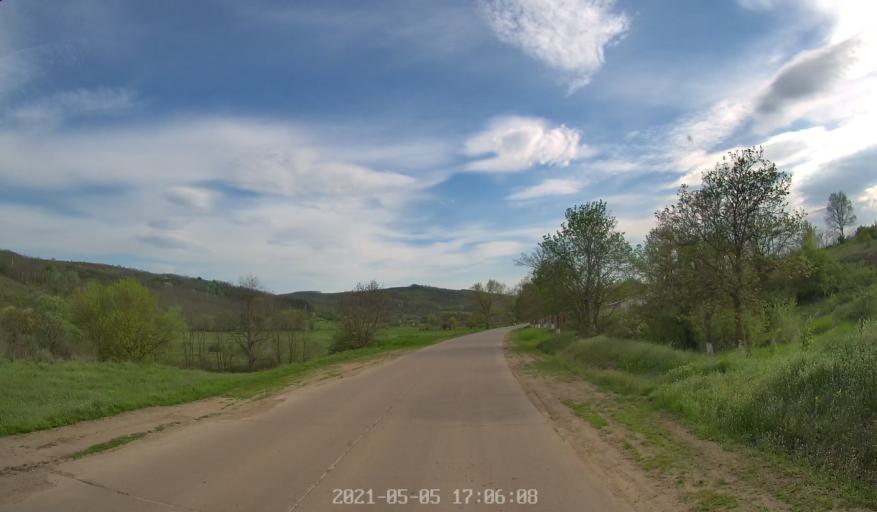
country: MD
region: Chisinau
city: Vadul lui Voda
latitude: 47.0232
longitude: 29.1403
